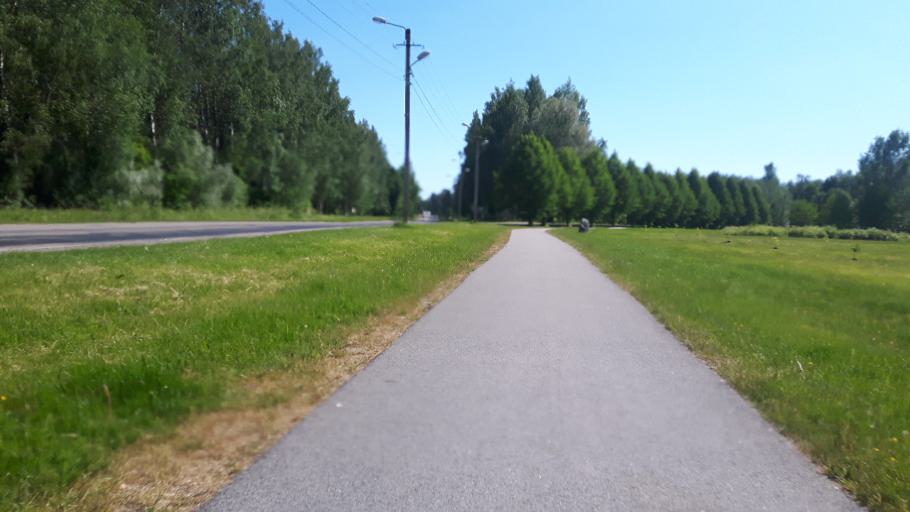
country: EE
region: Paernumaa
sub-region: Paikuse vald
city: Paikuse
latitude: 58.3956
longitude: 24.6409
